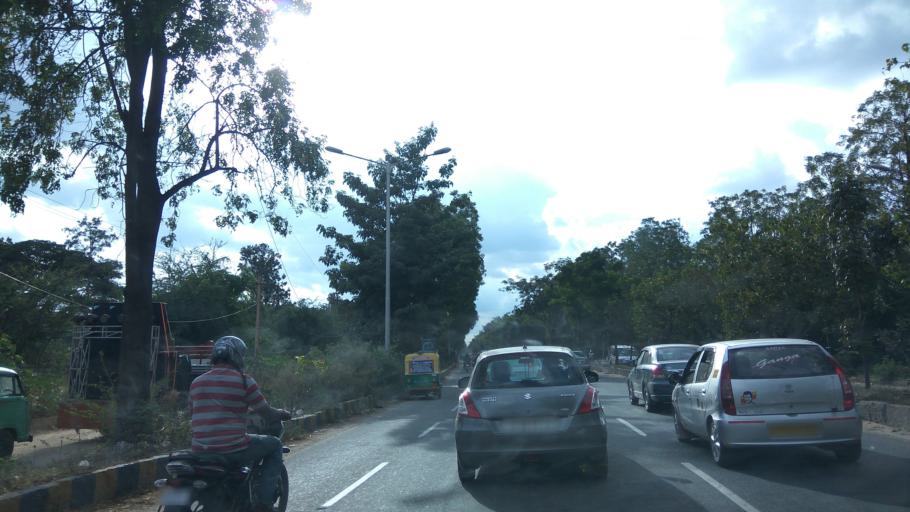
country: IN
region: Karnataka
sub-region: Bangalore Urban
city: Yelahanka
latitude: 13.0436
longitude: 77.6069
